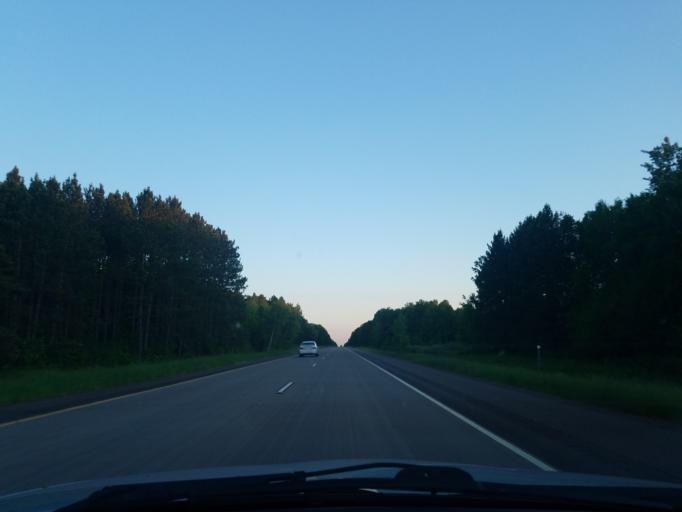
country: US
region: Minnesota
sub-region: Pine County
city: Sandstone
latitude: 46.0855
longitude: -92.8976
